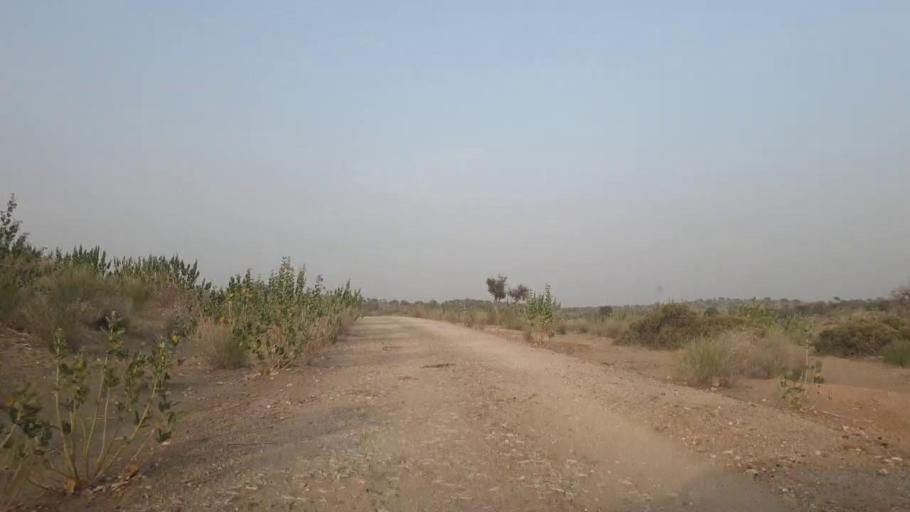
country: PK
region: Sindh
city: Chor
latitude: 25.5168
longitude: 69.9474
